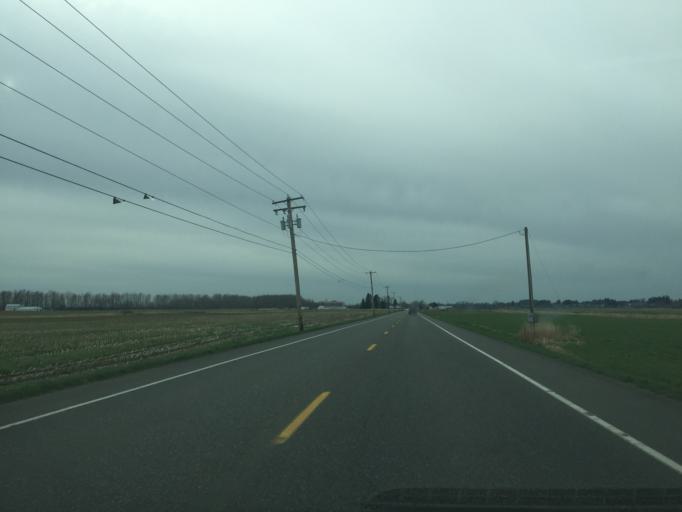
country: US
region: Washington
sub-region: Whatcom County
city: Lynden
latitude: 48.9420
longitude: -122.3961
